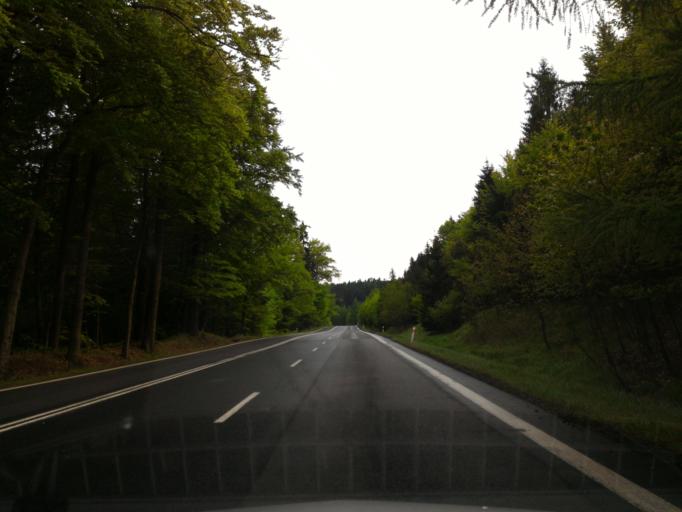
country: CZ
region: Ustecky
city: Dolni Podluzi
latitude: 50.8457
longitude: 14.5907
